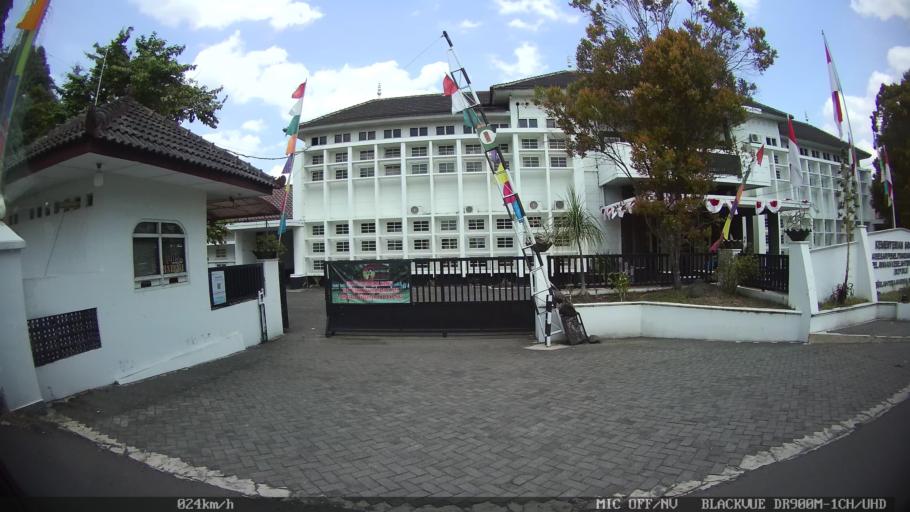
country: ID
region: Daerah Istimewa Yogyakarta
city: Gamping Lor
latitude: -7.8084
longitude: 110.3434
